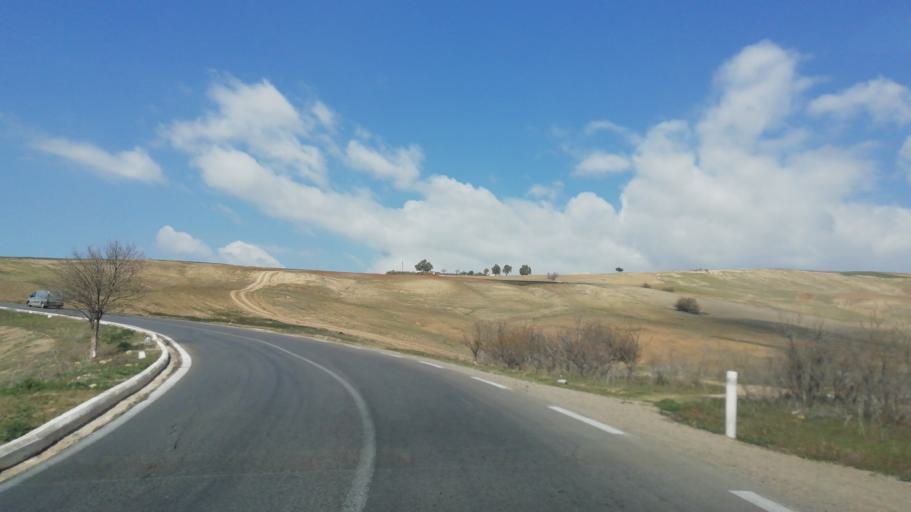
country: DZ
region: Mascara
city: Mascara
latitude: 35.5425
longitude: 0.1121
